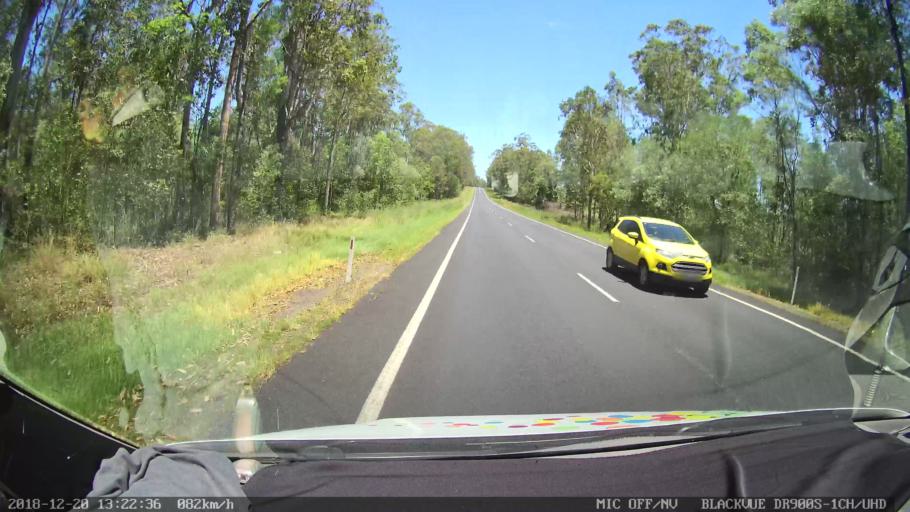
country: AU
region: New South Wales
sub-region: Richmond Valley
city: Casino
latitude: -29.0936
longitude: 153.0014
